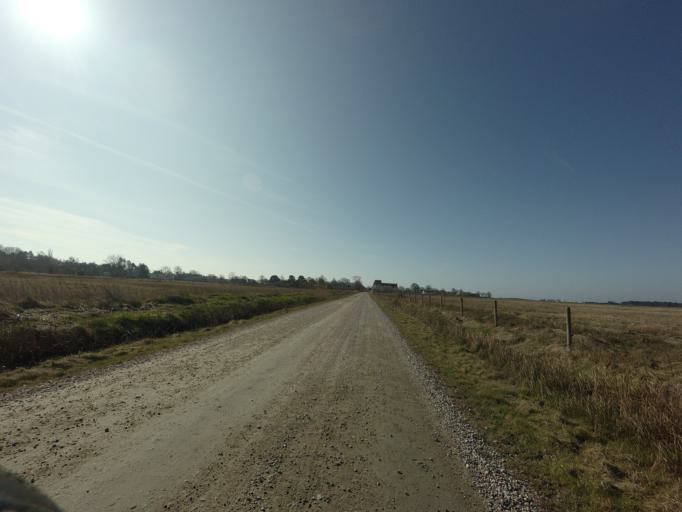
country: SE
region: Skane
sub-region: Vellinge Kommun
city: Skanor med Falsterbo
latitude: 55.4236
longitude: 12.8538
